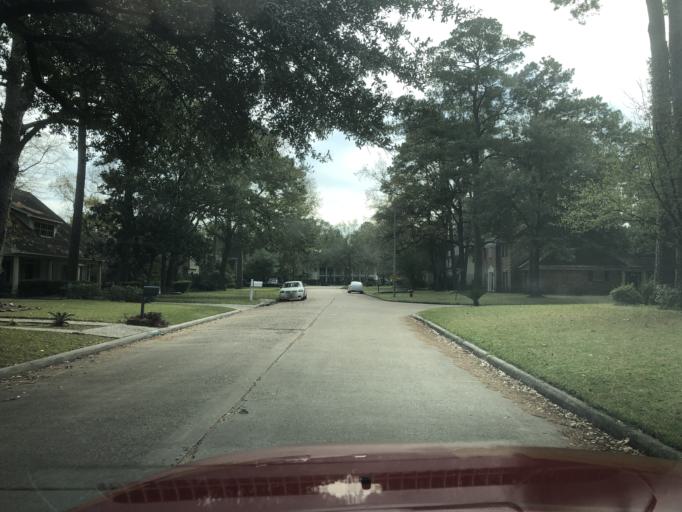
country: US
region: Texas
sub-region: Harris County
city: Spring
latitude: 30.0186
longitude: -95.4625
